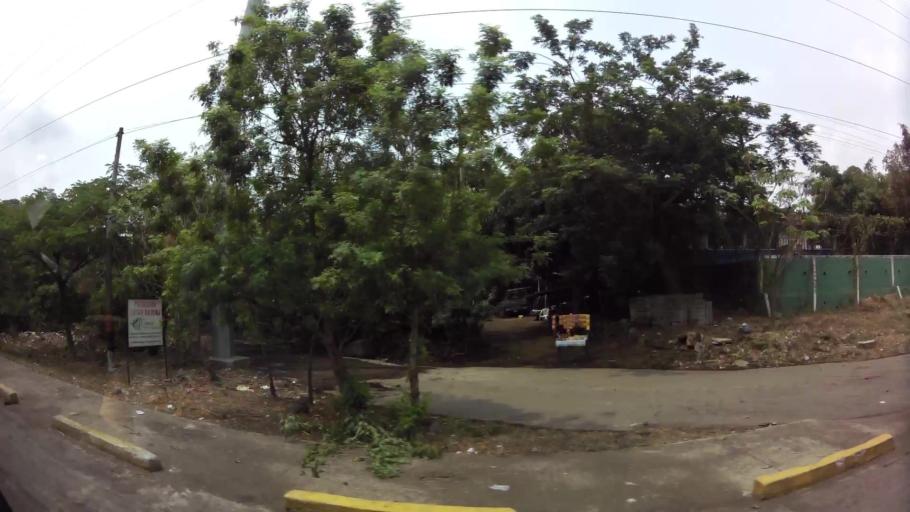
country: NI
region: Chinandega
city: Chinandega
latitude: 12.6380
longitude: -87.1243
